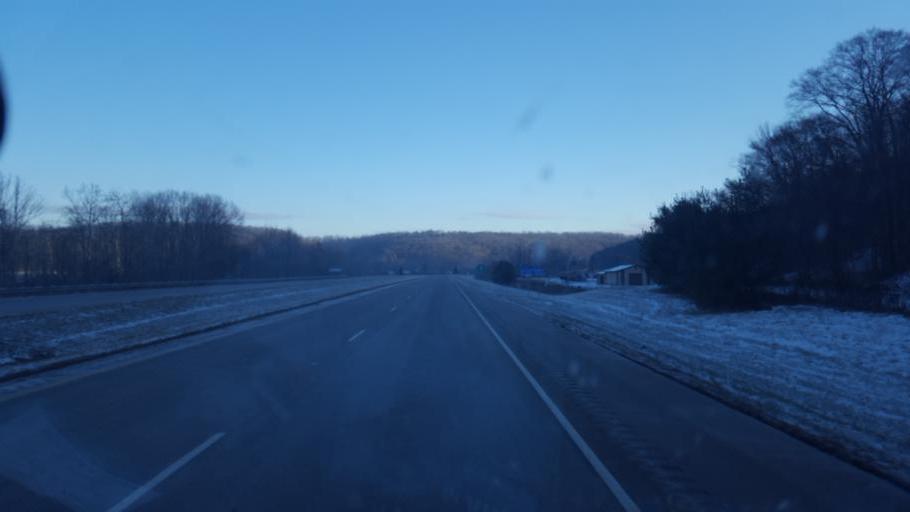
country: US
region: Ohio
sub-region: Pike County
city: Piketon
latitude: 39.0551
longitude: -83.1227
